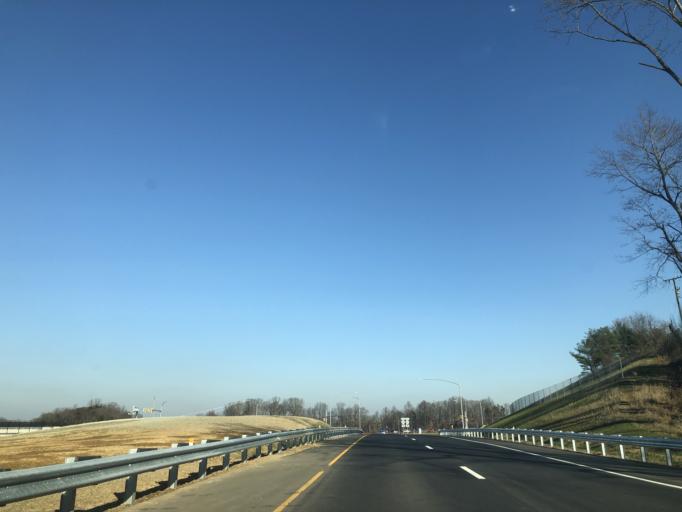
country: US
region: Virginia
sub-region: Stafford County
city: Stafford
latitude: 38.4184
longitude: -77.4232
